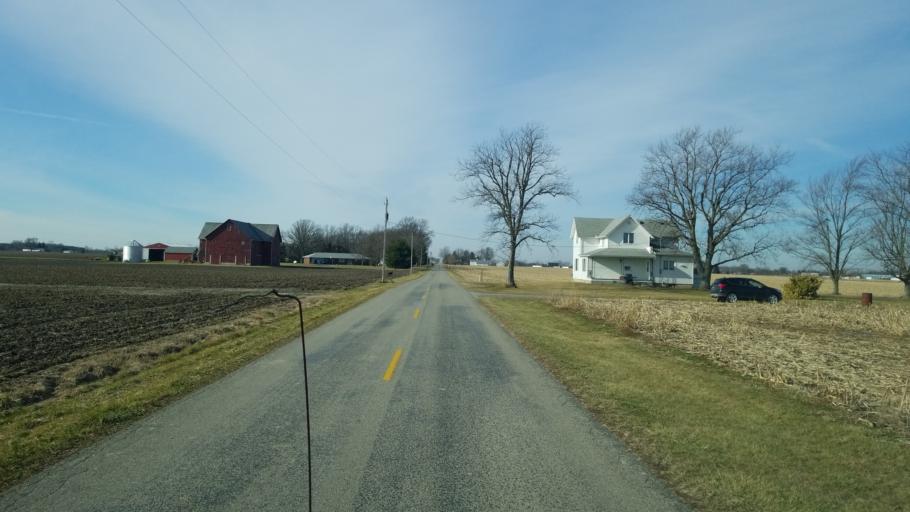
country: US
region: Ohio
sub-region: Allen County
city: Bluffton
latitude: 40.8631
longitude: -83.9081
